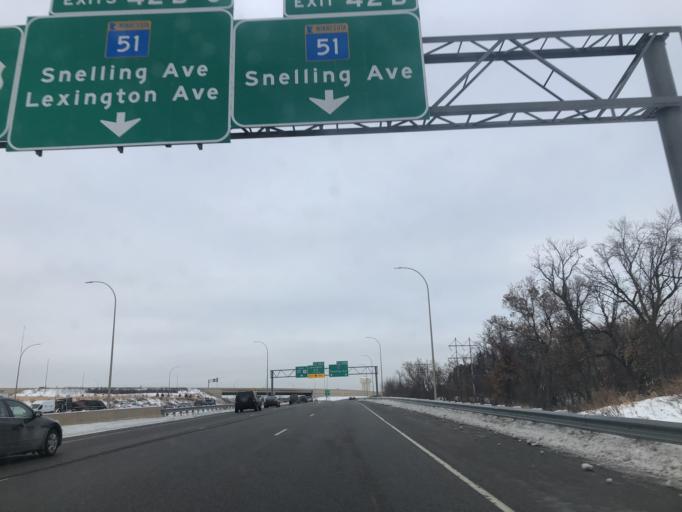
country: US
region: Minnesota
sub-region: Ramsey County
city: Arden Hills
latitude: 45.0638
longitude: -93.1628
